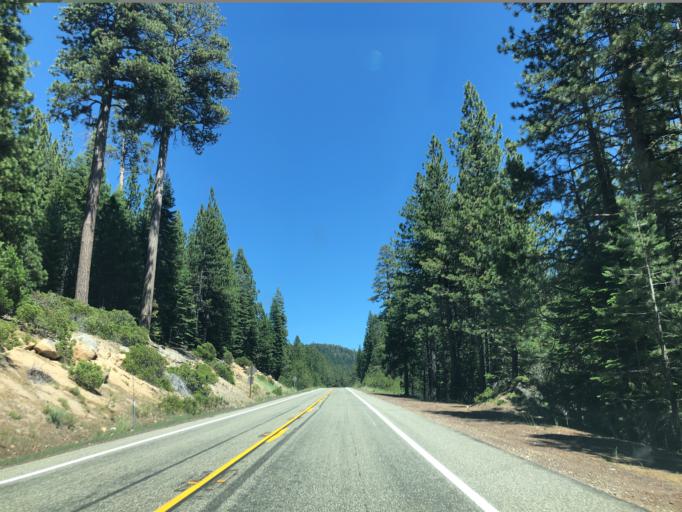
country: US
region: California
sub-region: Shasta County
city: Shingletown
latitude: 40.5395
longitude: -121.5899
